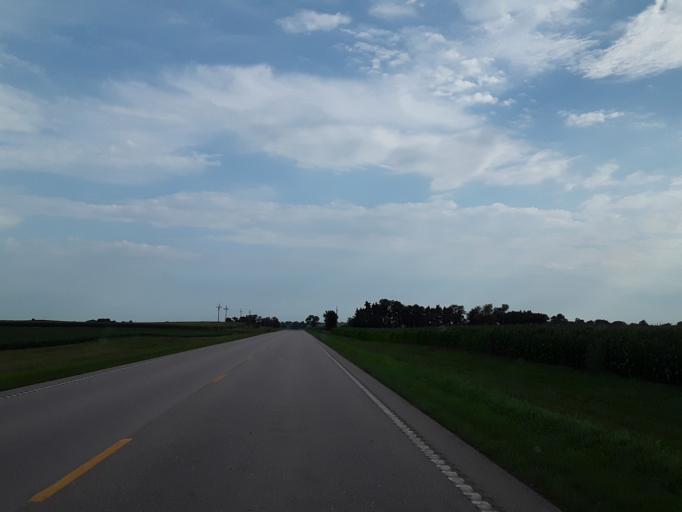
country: US
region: Nebraska
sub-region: Saunders County
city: Ashland
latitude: 41.1062
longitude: -96.4259
